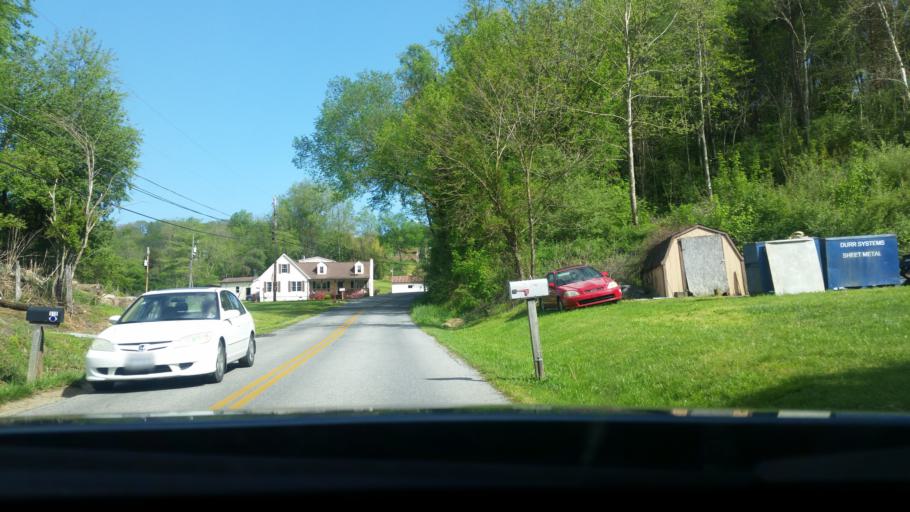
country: US
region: Virginia
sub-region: Giles County
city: Pembroke
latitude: 37.3156
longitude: -80.6338
